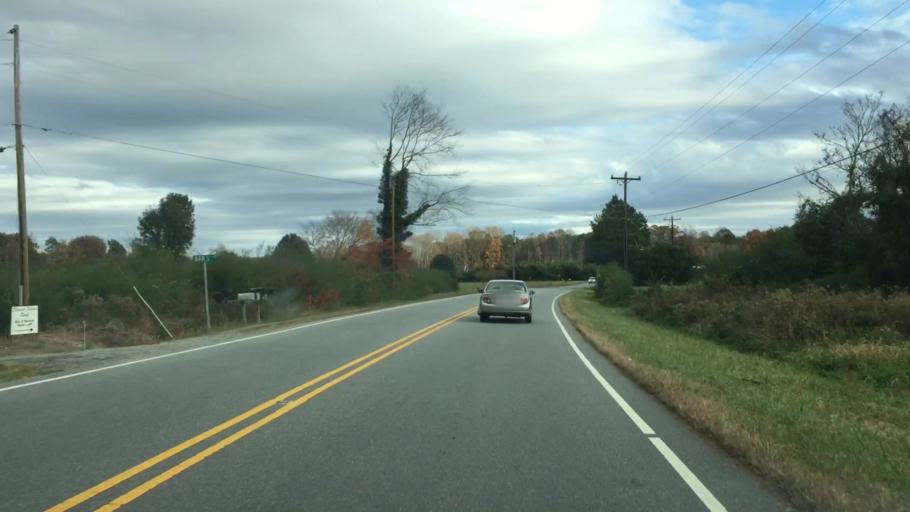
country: US
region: North Carolina
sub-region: Guilford County
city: Summerfield
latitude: 36.2772
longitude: -79.8043
